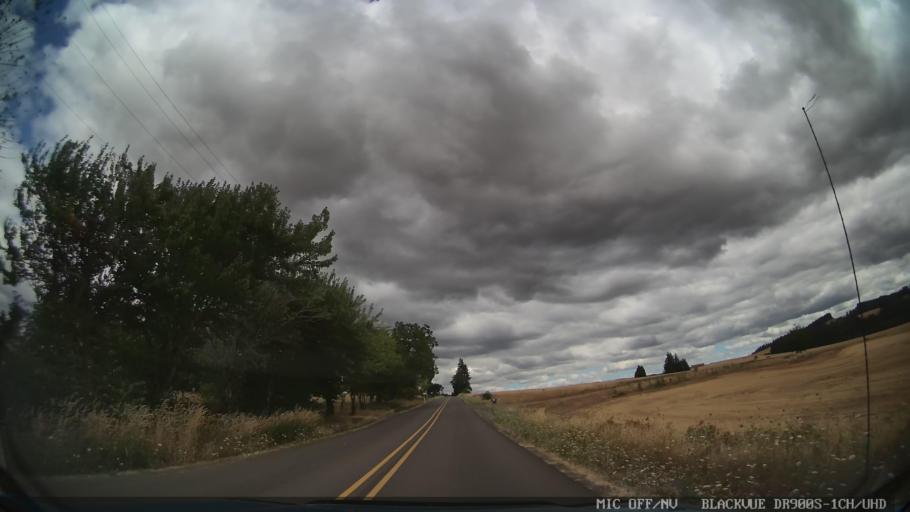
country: US
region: Oregon
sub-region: Marion County
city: Sublimity
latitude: 44.8724
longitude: -122.7275
